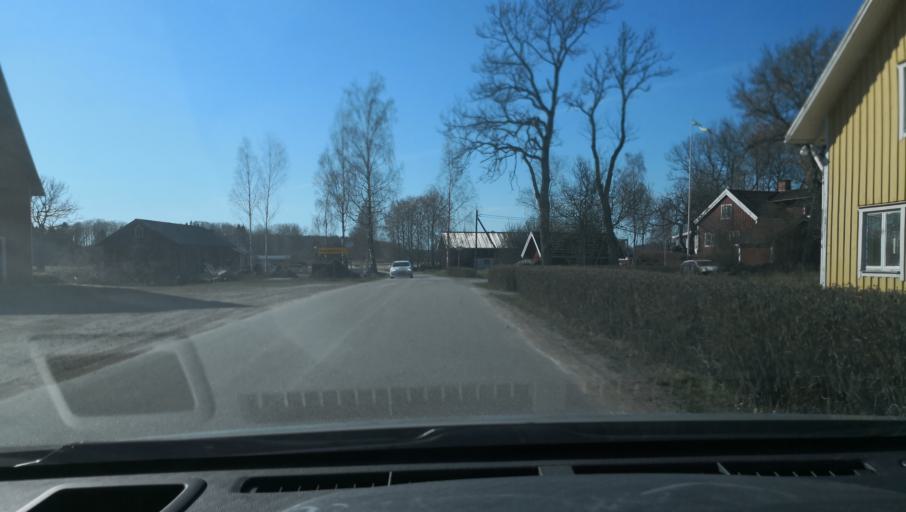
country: SE
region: Vaestmanland
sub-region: Sala Kommun
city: Sala
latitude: 60.0854
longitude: 16.5239
